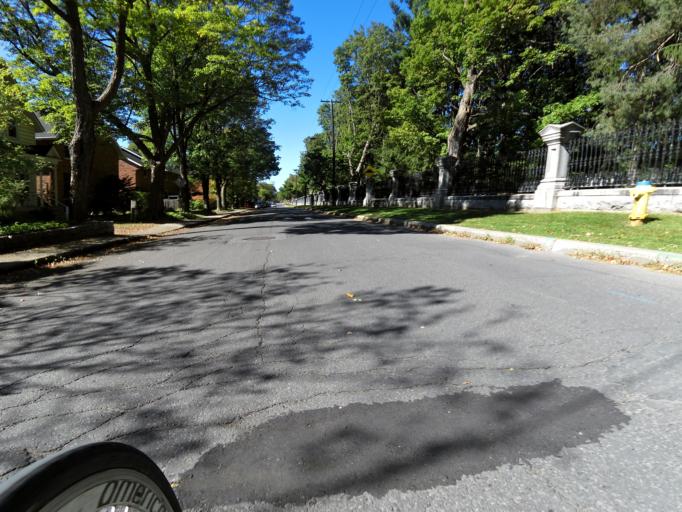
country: CA
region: Ontario
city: Ottawa
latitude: 45.4412
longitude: -75.6842
